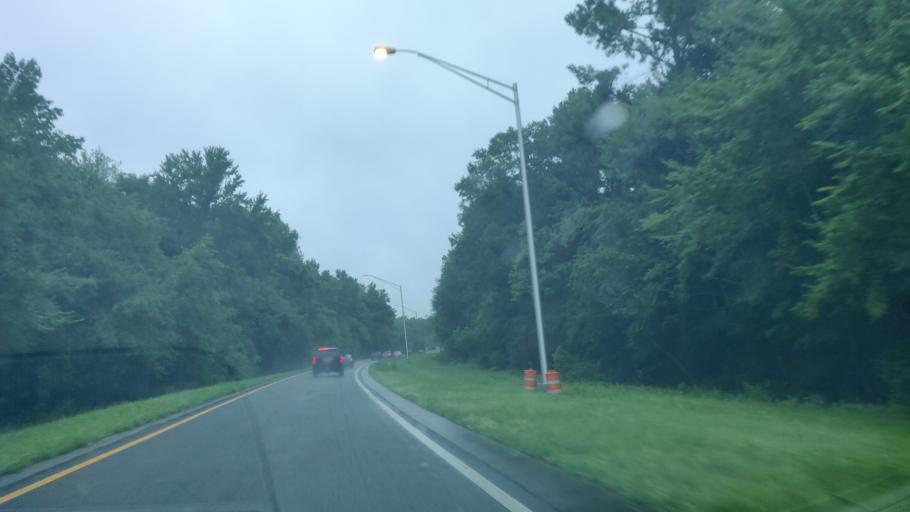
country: US
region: Florida
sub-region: Duval County
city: Jacksonville
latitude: 30.3134
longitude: -81.7723
